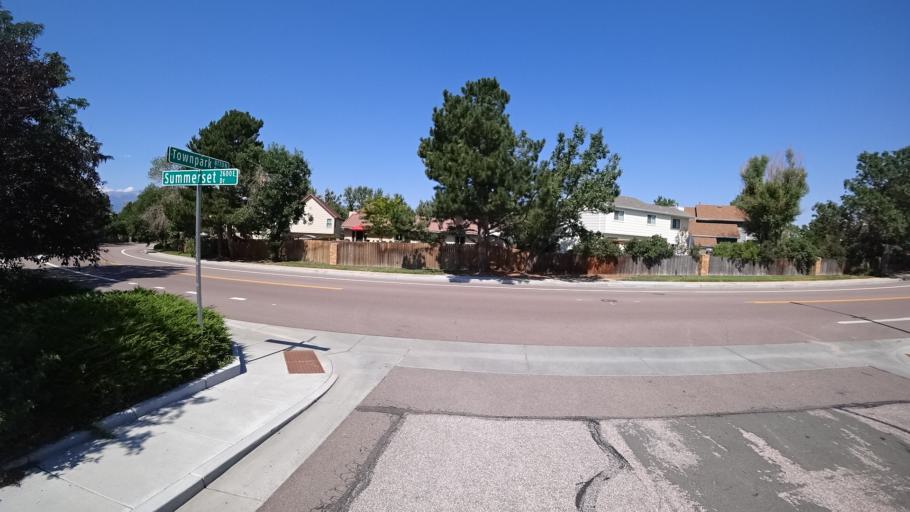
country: US
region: Colorado
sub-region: El Paso County
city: Air Force Academy
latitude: 38.9581
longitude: -104.7776
